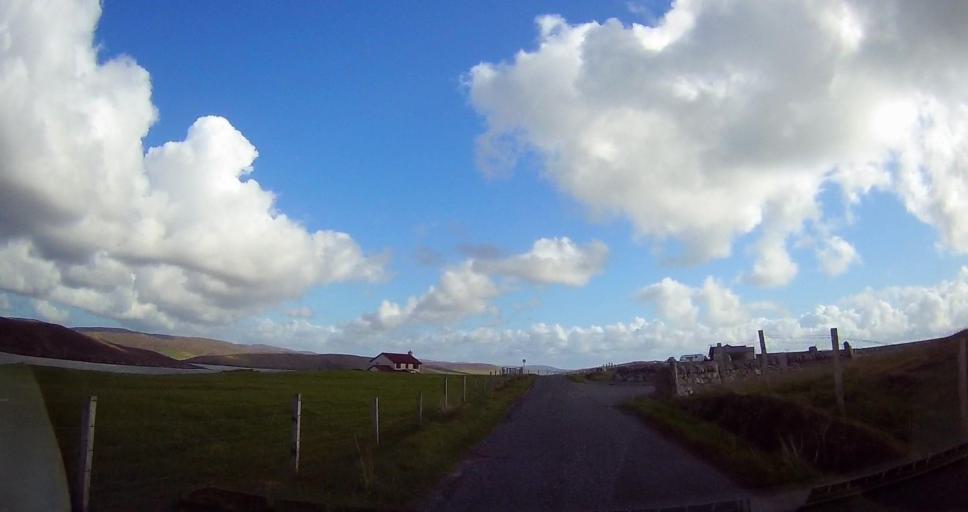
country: GB
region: Scotland
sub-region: Shetland Islands
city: Lerwick
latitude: 60.3644
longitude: -1.3825
